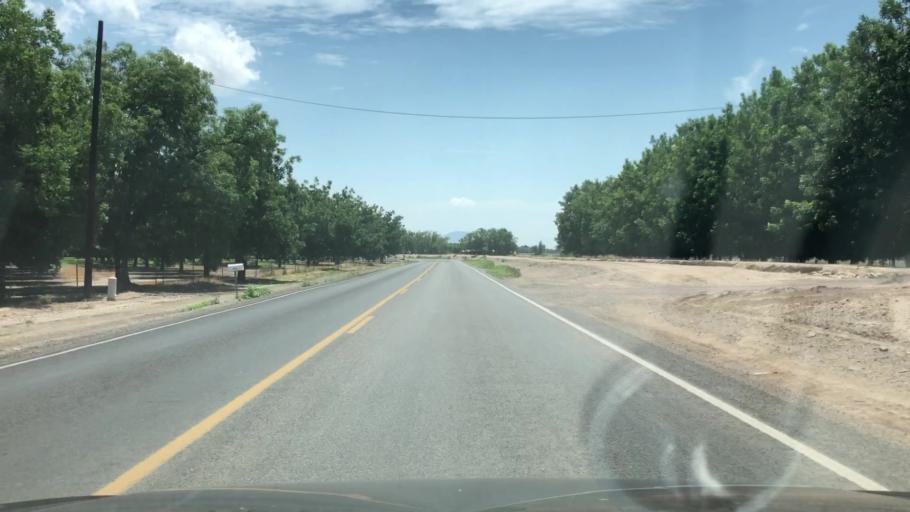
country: US
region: New Mexico
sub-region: Dona Ana County
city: La Union
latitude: 32.0057
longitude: -106.6618
